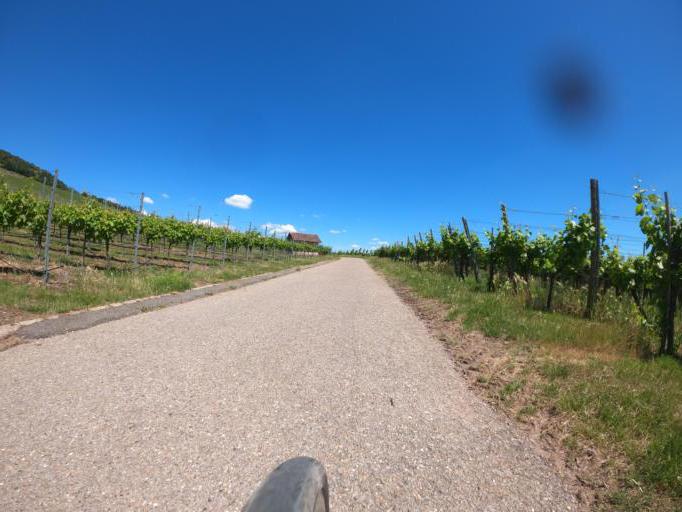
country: DE
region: Baden-Wuerttemberg
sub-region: Regierungsbezirk Stuttgart
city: Sersheim
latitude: 48.9895
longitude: 8.9888
